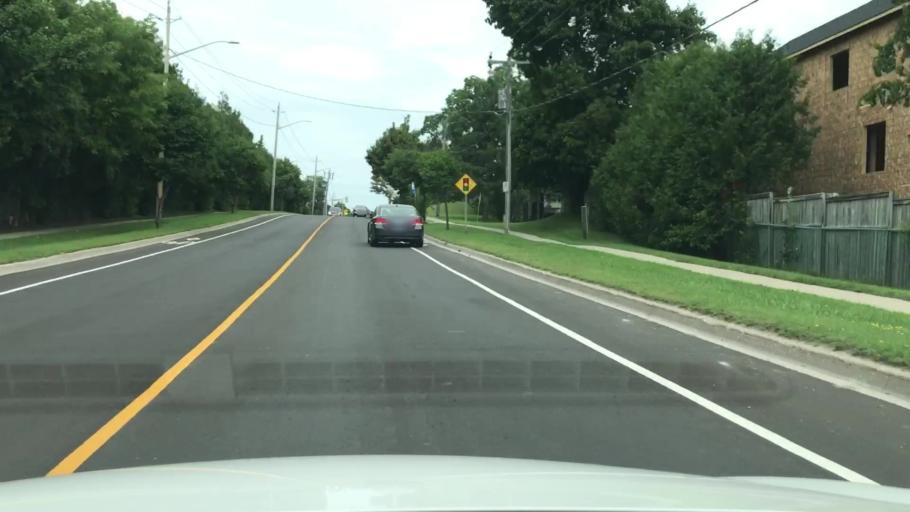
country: CA
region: Ontario
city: Newmarket
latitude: 44.0719
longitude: -79.4587
